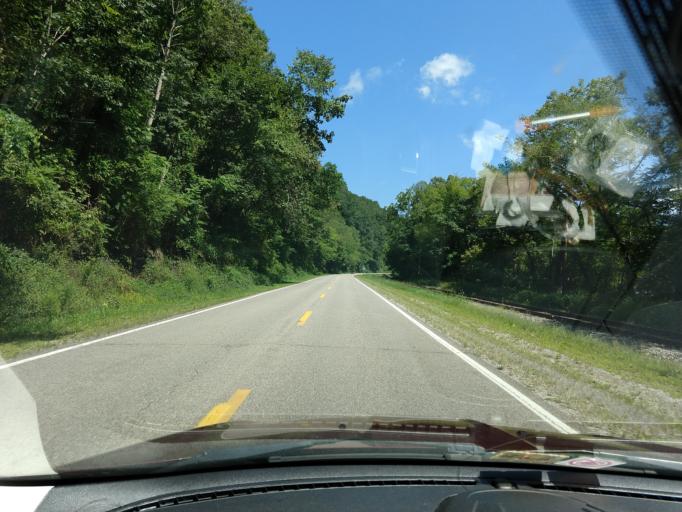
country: US
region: West Virginia
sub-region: Kanawha County
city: Montgomery
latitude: 38.1305
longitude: -81.2206
